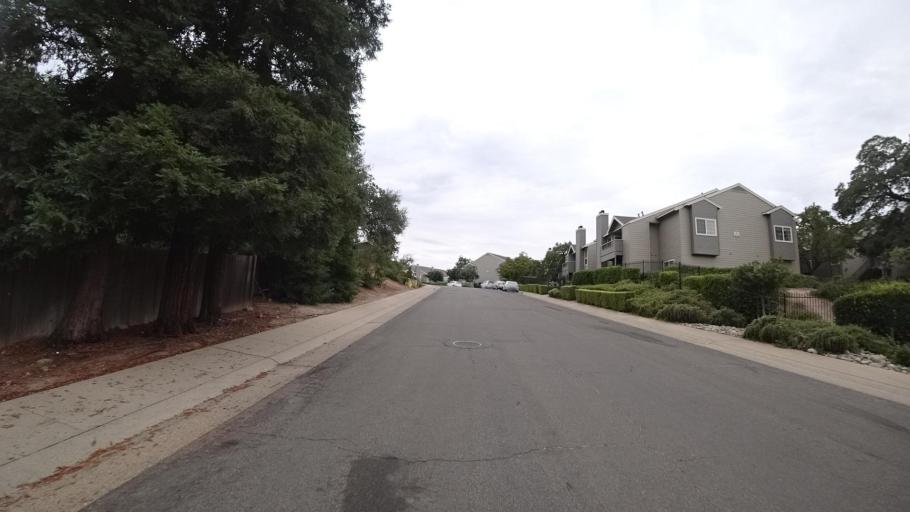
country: US
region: California
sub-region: Placer County
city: Rocklin
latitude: 38.7912
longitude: -121.2570
